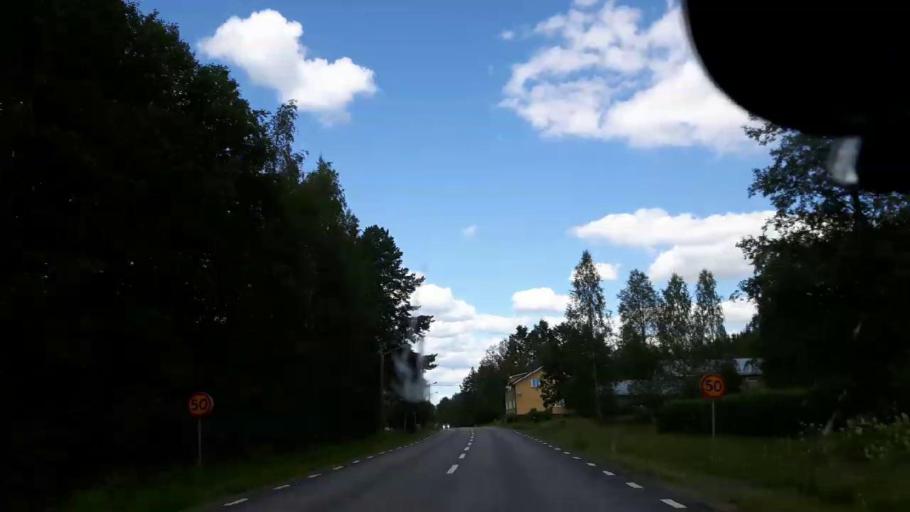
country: SE
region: Jaemtland
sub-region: Ragunda Kommun
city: Hammarstrand
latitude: 62.9985
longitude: 16.6767
